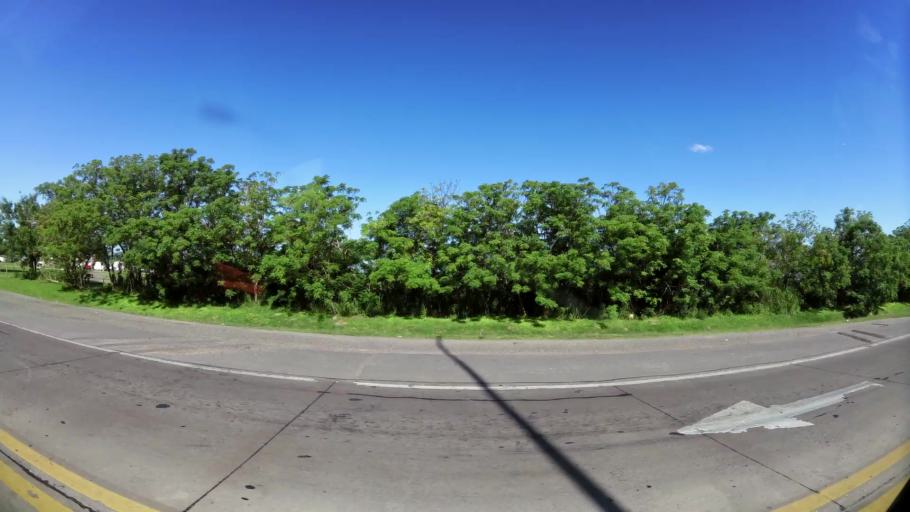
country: AR
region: Santa Fe
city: Rafaela
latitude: -31.2843
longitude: -61.5133
